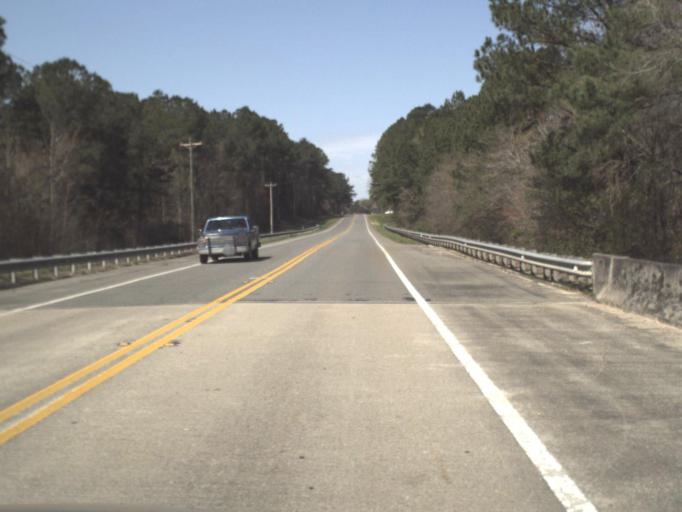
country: US
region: Florida
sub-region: Gadsden County
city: Quincy
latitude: 30.5877
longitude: -84.4971
